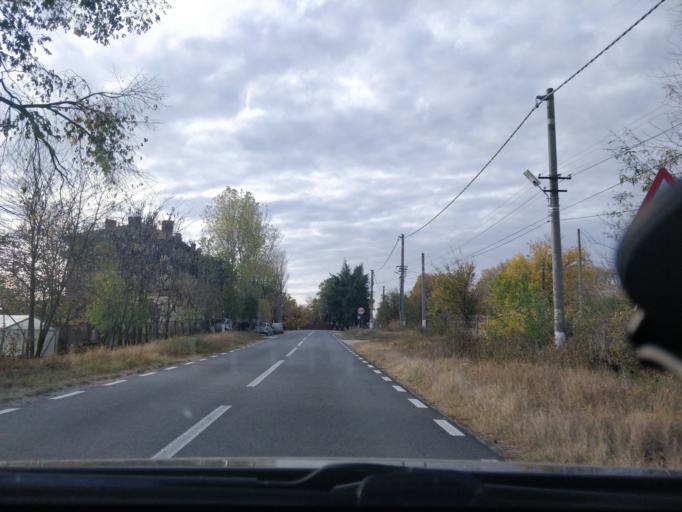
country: RO
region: Giurgiu
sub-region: Comuna Bucsani
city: Bucsani
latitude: 44.3676
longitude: 25.6626
